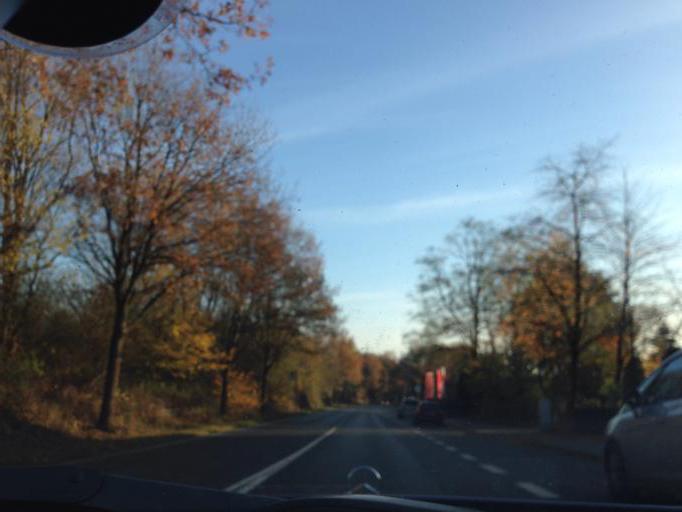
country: DE
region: Schleswig-Holstein
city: Reinbek
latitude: 53.5596
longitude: 10.2497
